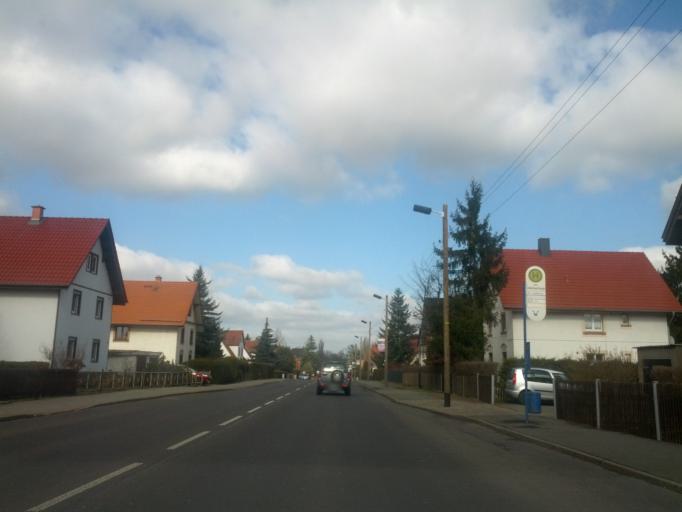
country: DE
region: Thuringia
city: Gotha
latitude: 50.9327
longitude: 10.7152
